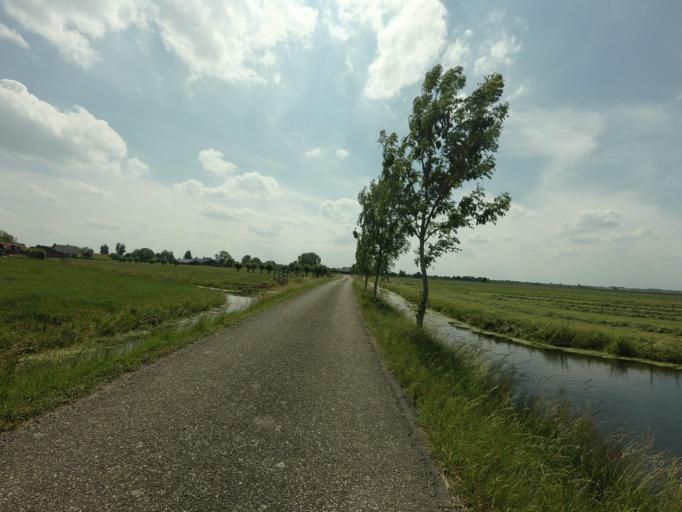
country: NL
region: Utrecht
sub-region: Gemeente Lopik
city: Lopik
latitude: 51.9549
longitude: 4.9215
